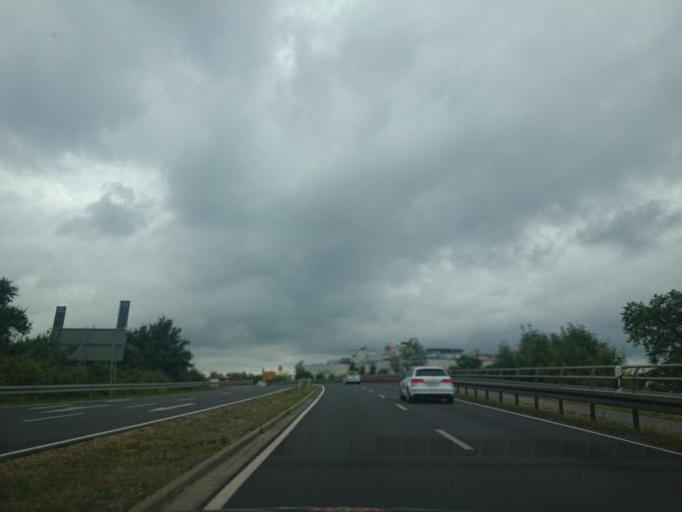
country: DE
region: Brandenburg
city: Wildau
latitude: 52.3118
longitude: 13.6027
